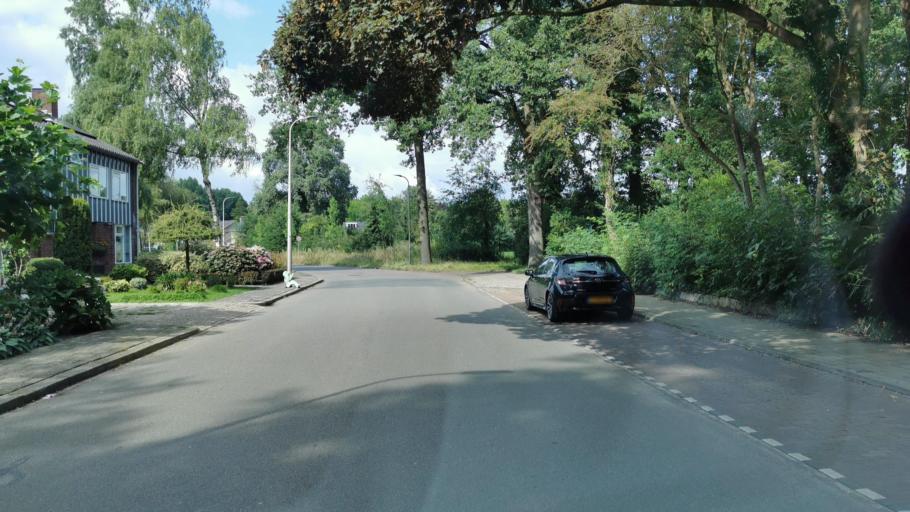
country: NL
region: Overijssel
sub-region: Gemeente Enschede
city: Enschede
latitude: 52.2342
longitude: 6.8829
